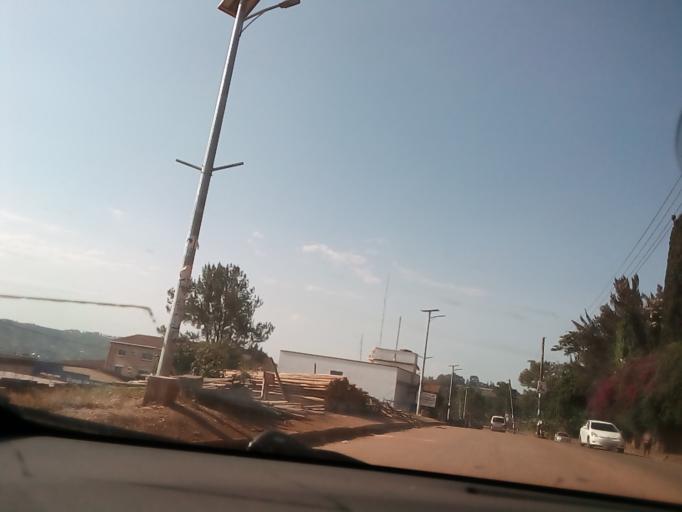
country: UG
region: Central Region
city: Masaka
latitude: -0.3458
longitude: 31.7373
